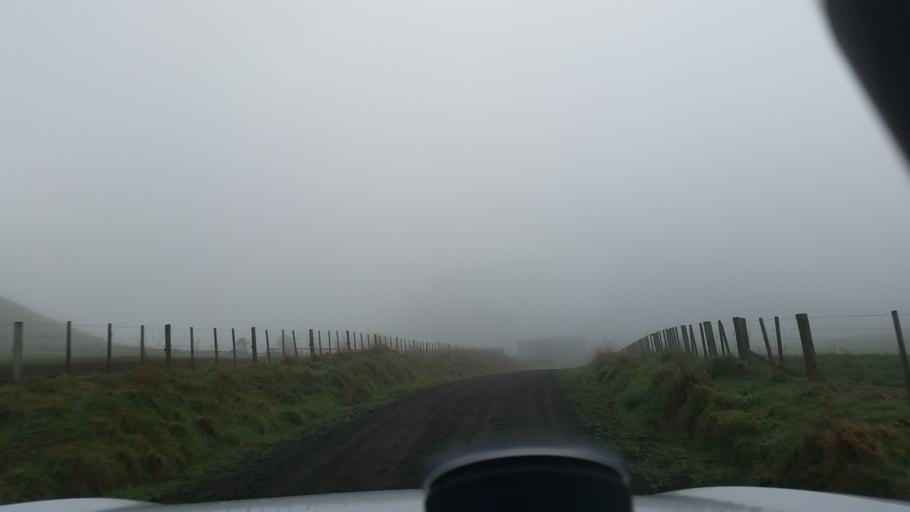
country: NZ
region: Taranaki
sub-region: South Taranaki District
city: Eltham
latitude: -39.4209
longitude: 174.4348
